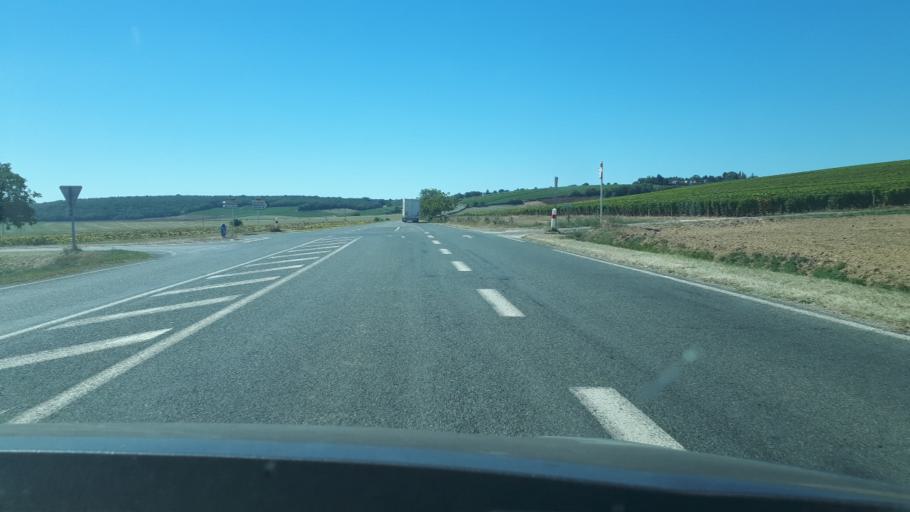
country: FR
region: Centre
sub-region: Departement du Cher
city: Sancerre
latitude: 47.2922
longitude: 2.7776
